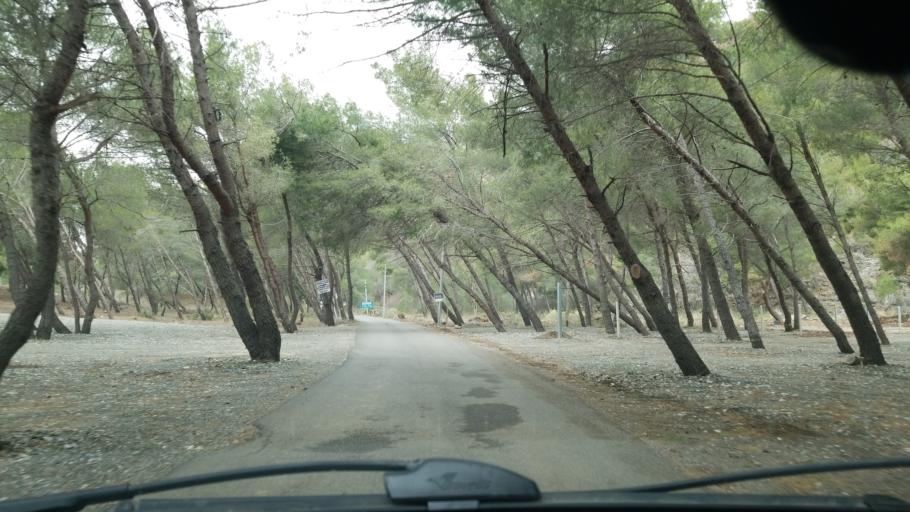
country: AL
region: Lezhe
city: Shengjin
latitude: 41.8228
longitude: 19.5612
